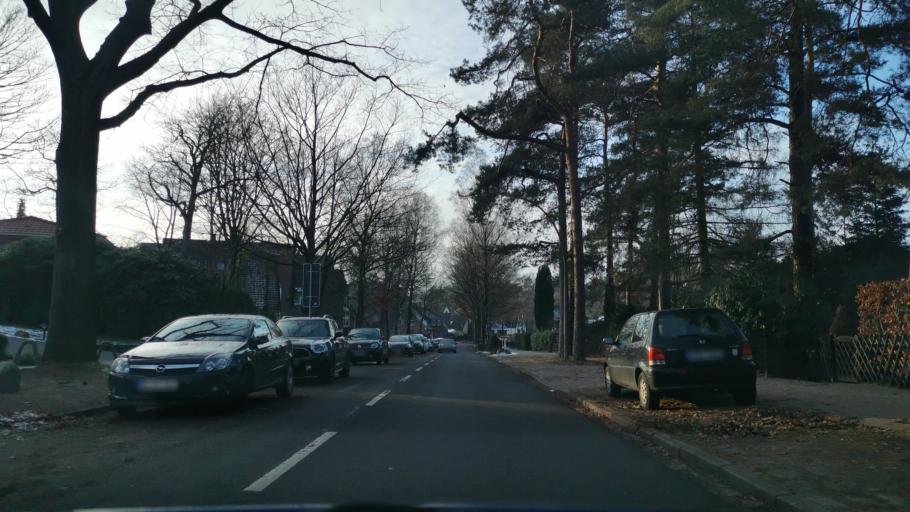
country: DE
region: Hamburg
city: Harburg
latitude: 53.4504
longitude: 9.9267
